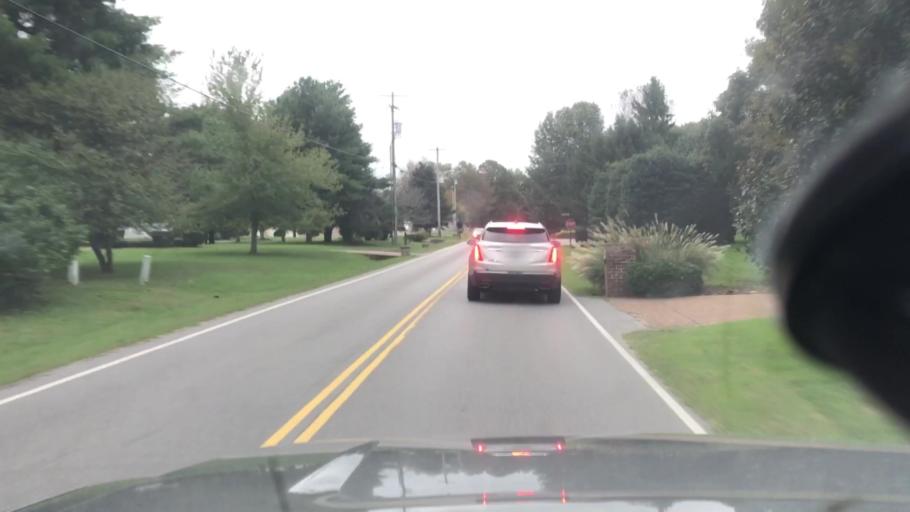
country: US
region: Tennessee
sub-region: Davidson County
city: Forest Hills
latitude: 36.0307
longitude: -86.8316
